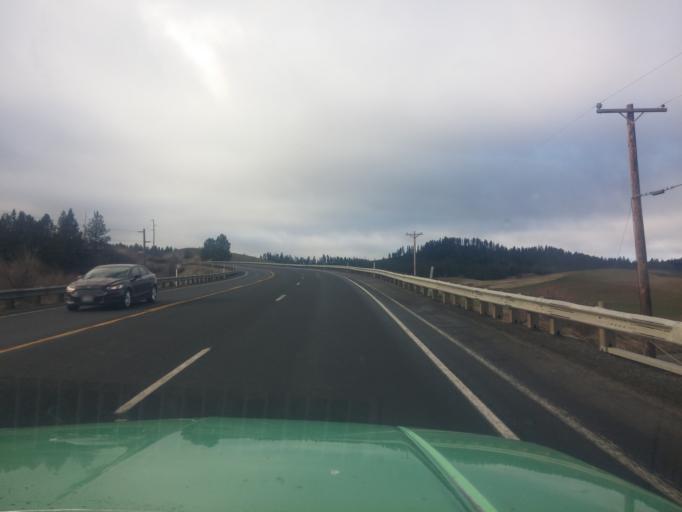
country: US
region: Idaho
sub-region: Latah County
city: Moscow
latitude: 46.8852
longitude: -117.0020
